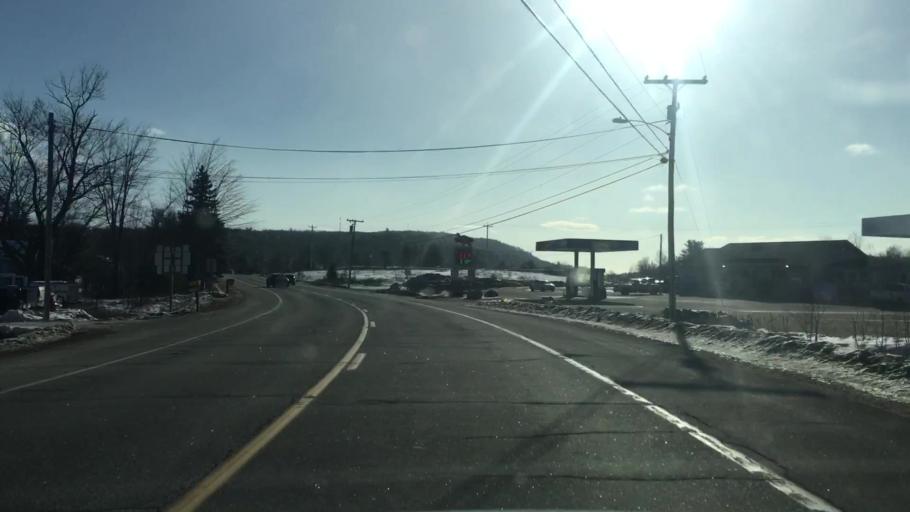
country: US
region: Maine
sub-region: Oxford County
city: West Paris
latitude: 44.3305
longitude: -70.5550
